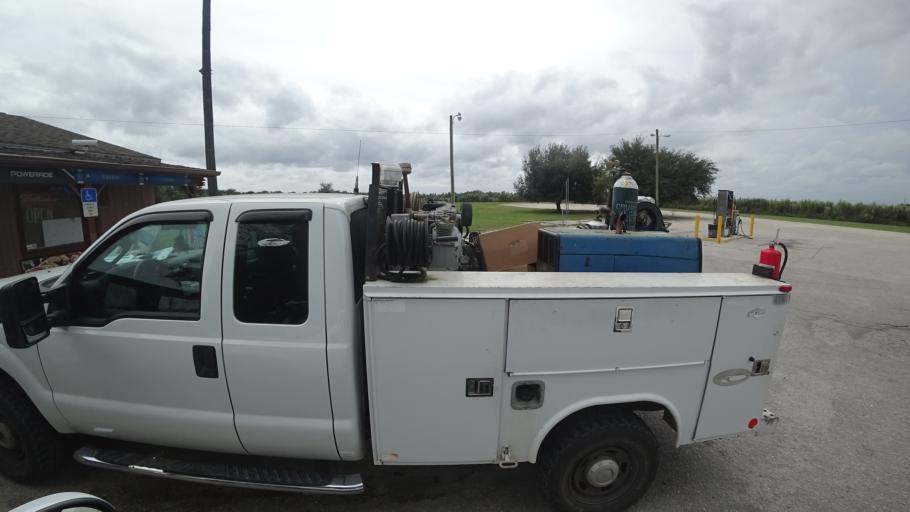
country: US
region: Florida
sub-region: Hillsborough County
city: Wimauma
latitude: 27.5882
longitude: -82.1542
